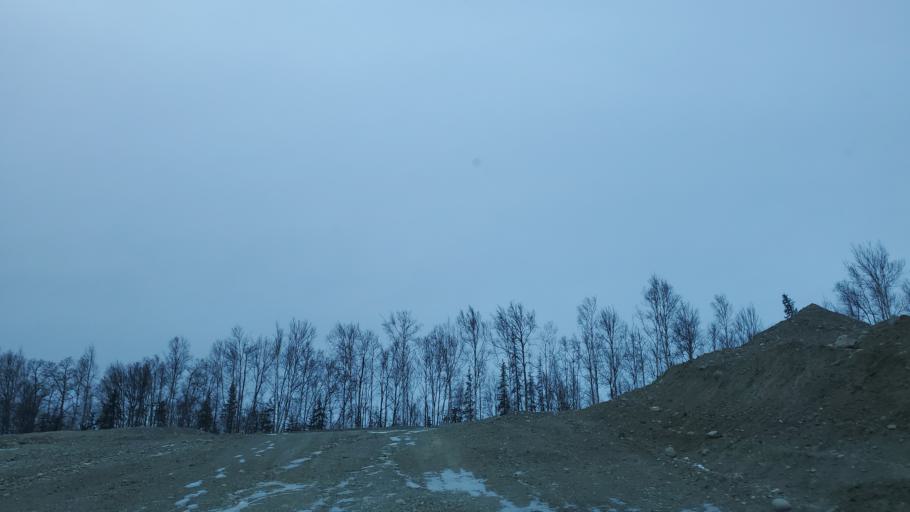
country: US
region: Alaska
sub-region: Matanuska-Susitna Borough
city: Gateway
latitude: 61.6543
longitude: -149.2354
